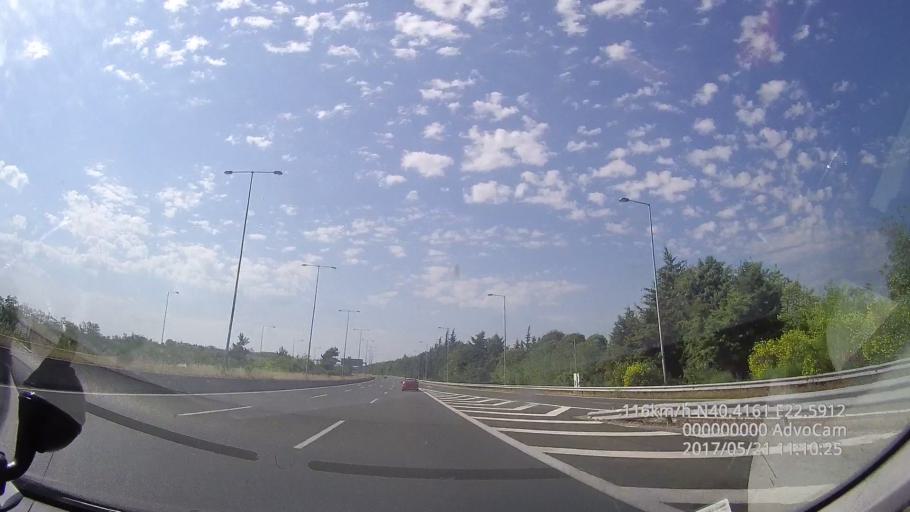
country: GR
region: Central Macedonia
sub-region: Nomos Pierias
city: Makrygialos
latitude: 40.4153
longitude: 22.5914
